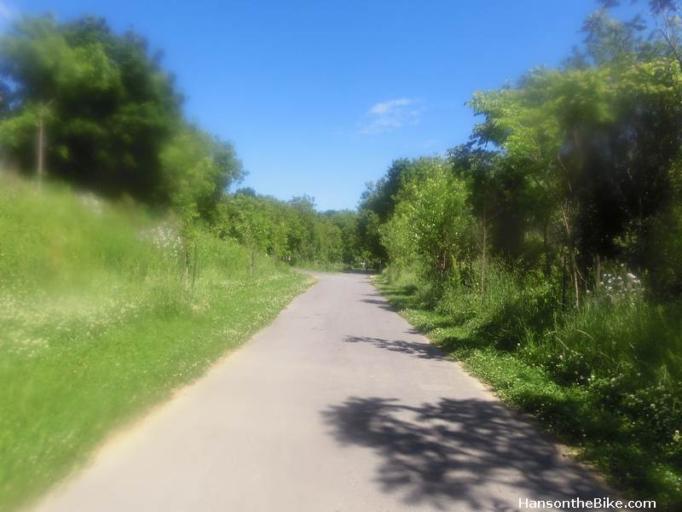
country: CA
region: Ontario
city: Kingston
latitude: 44.2469
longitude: -76.4848
